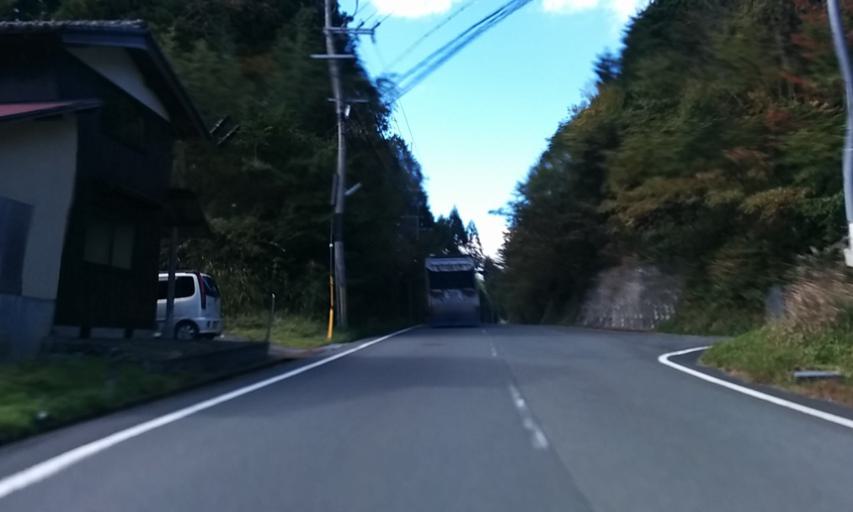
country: JP
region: Kyoto
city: Kameoka
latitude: 35.2058
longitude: 135.5898
